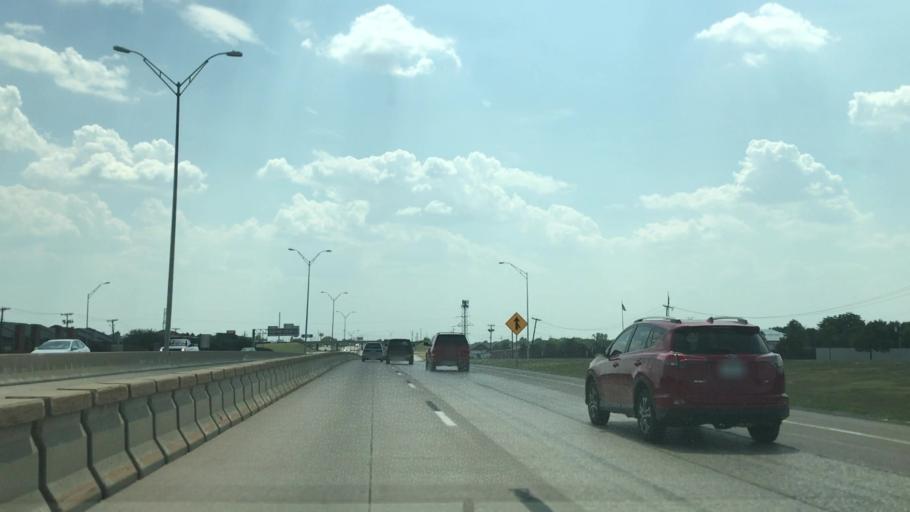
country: US
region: Texas
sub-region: Dallas County
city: Mesquite
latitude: 32.8213
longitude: -96.6331
